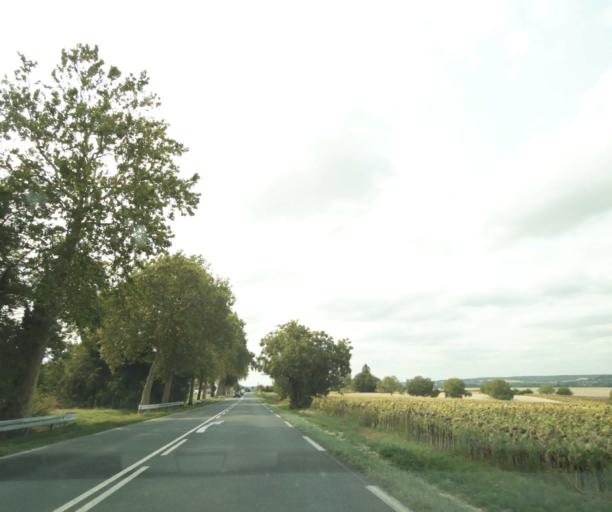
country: FR
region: Centre
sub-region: Departement de l'Indre
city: Buzancais
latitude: 46.9134
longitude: 1.3267
